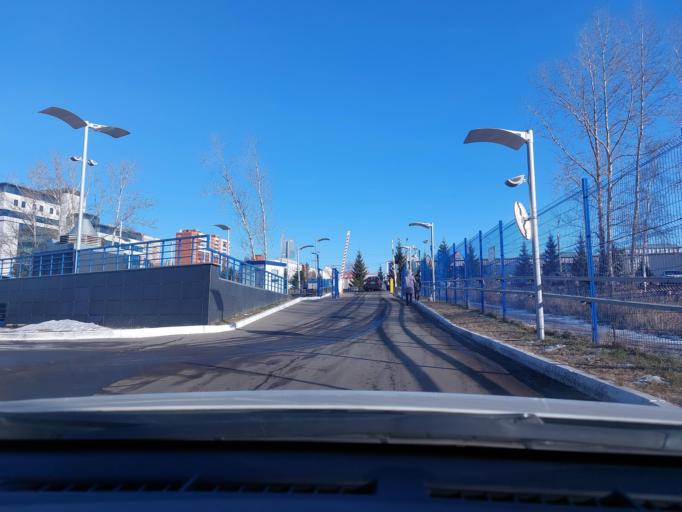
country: RU
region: Irkutsk
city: Dzerzhinsk
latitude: 52.2561
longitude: 104.3512
